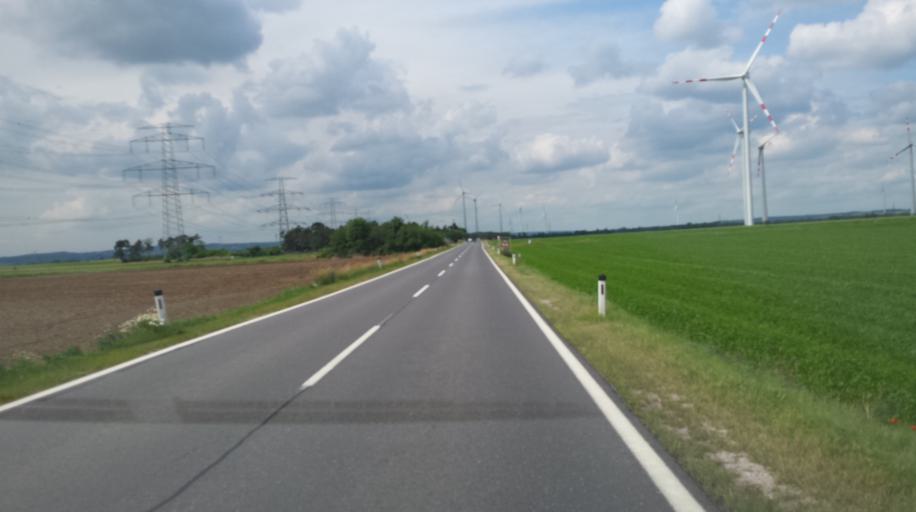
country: AT
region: Lower Austria
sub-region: Politischer Bezirk Ganserndorf
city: Aderklaa
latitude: 48.3147
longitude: 16.5341
